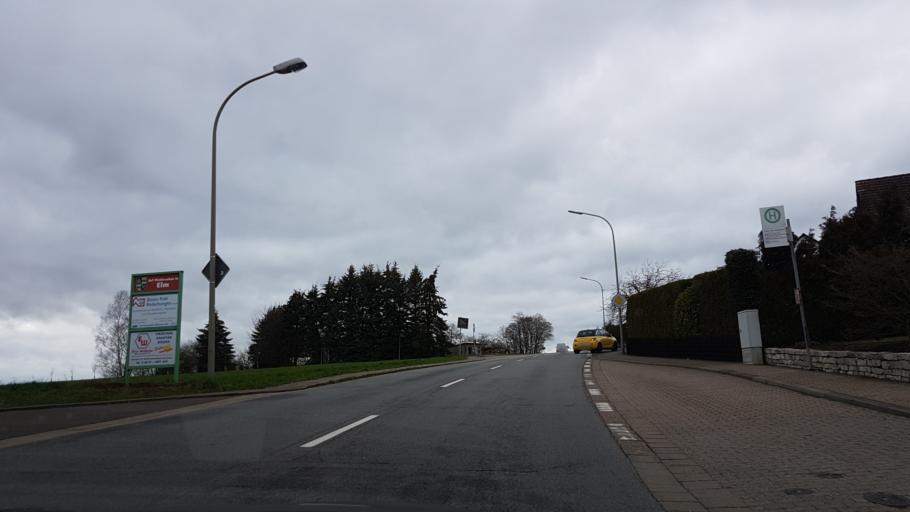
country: DE
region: Saarland
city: Schwalbach
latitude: 49.3074
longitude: 6.8485
